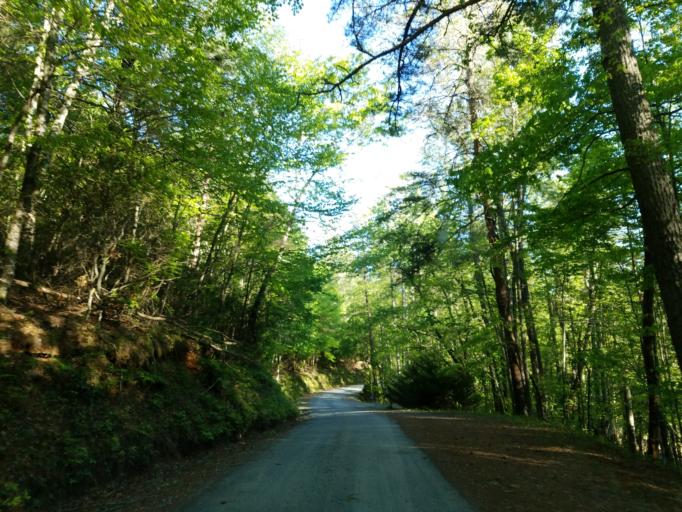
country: US
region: Georgia
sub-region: Fannin County
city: Blue Ridge
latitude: 34.7510
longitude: -84.2671
